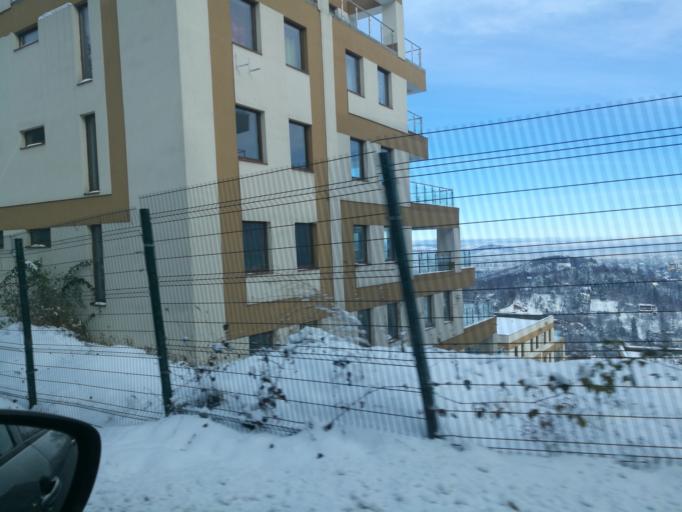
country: RO
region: Brasov
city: Brasov
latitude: 45.6383
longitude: 25.5638
